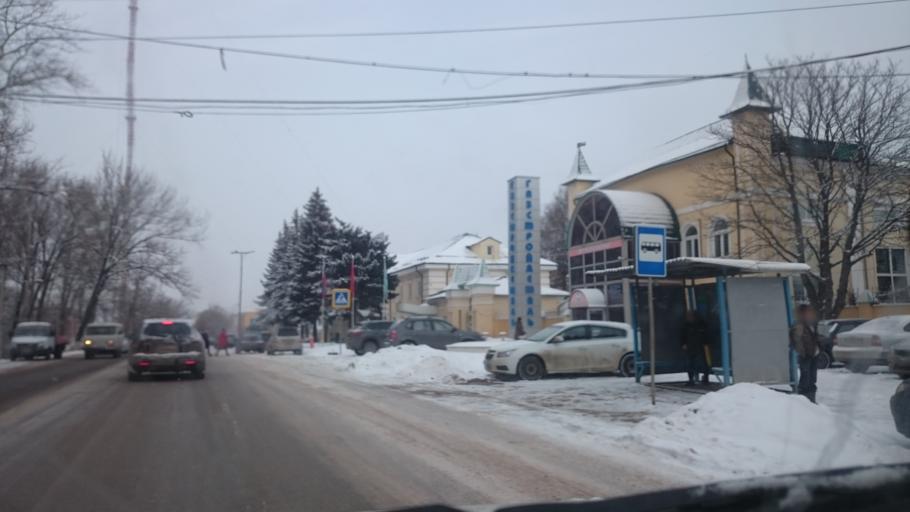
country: RU
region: Tula
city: Mendeleyevskiy
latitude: 54.1357
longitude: 37.5903
